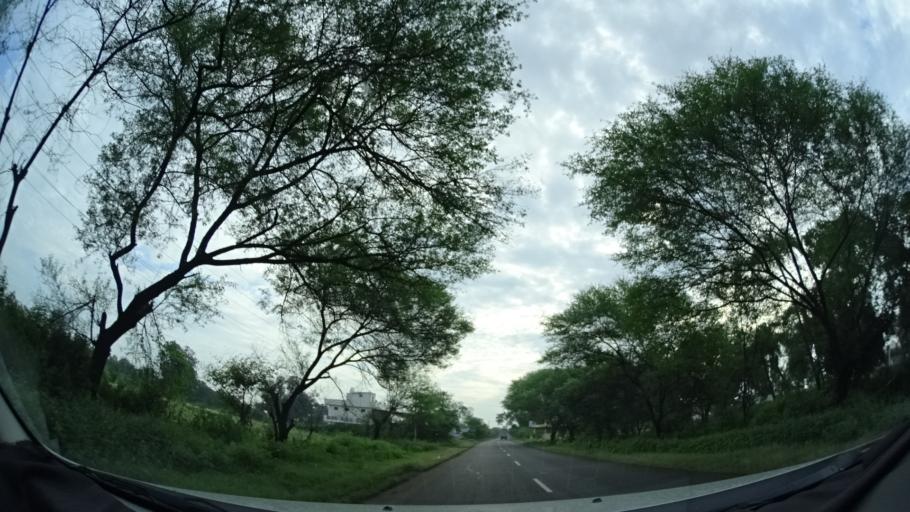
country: IN
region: Madhya Pradesh
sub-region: Sehore
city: Sehore
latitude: 23.2380
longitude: 77.2314
